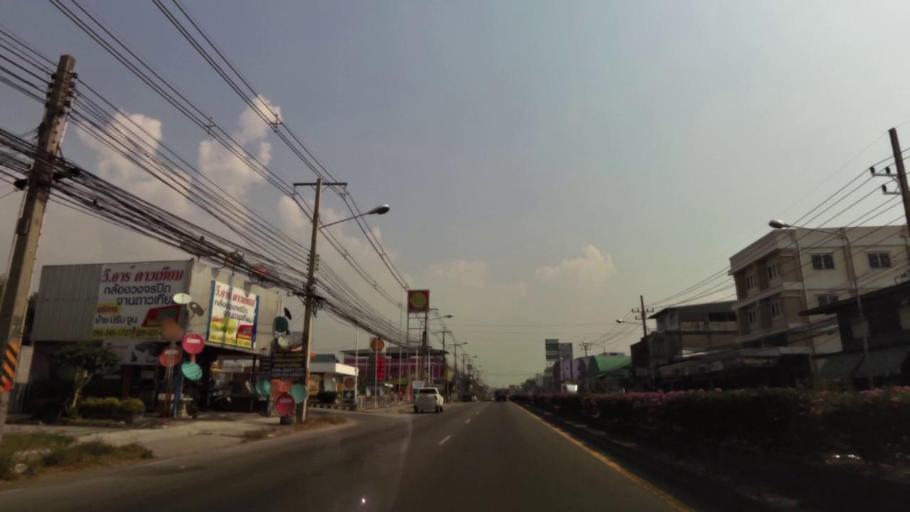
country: TH
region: Chon Buri
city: Chon Buri
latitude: 13.3515
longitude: 101.0084
